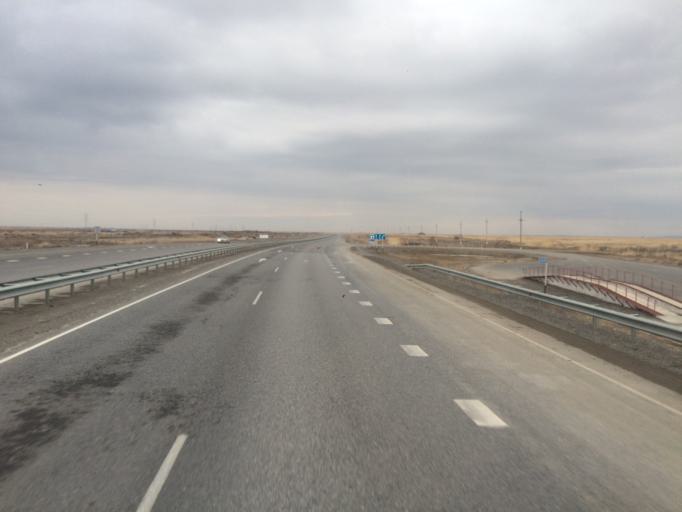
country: KZ
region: Qyzylorda
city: Shieli
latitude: 44.1559
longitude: 66.9329
